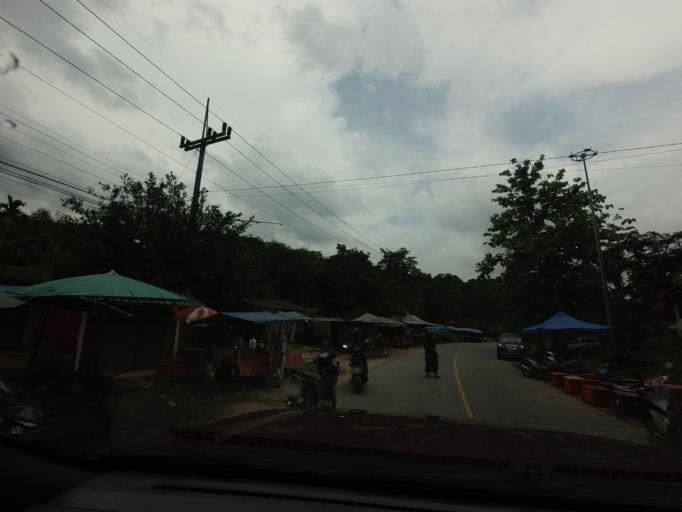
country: TH
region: Yala
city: Than To
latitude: 6.2023
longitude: 101.2375
